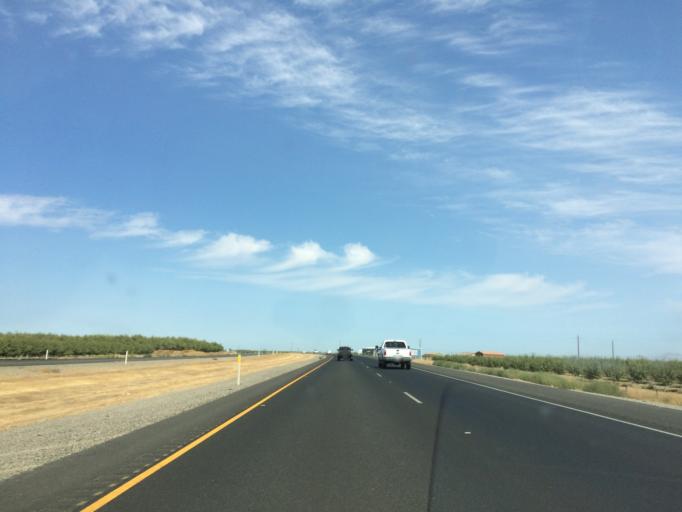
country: US
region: California
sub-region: Yolo County
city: Dunnigan
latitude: 38.9310
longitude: -122.0023
